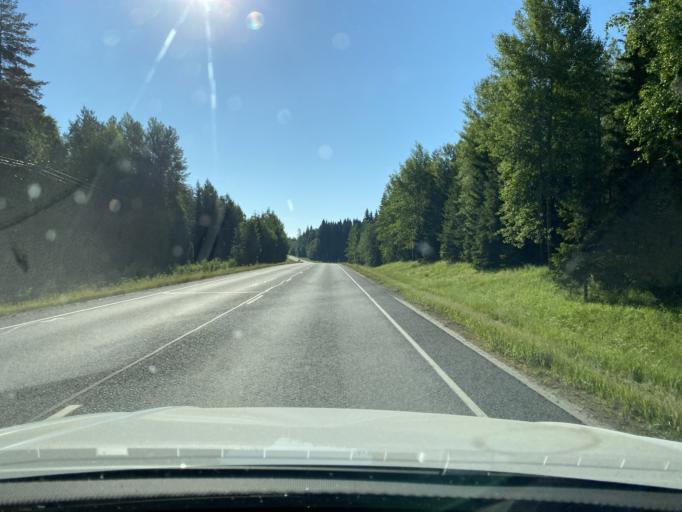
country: FI
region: Haeme
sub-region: Forssa
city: Tammela
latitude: 60.8274
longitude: 23.8974
